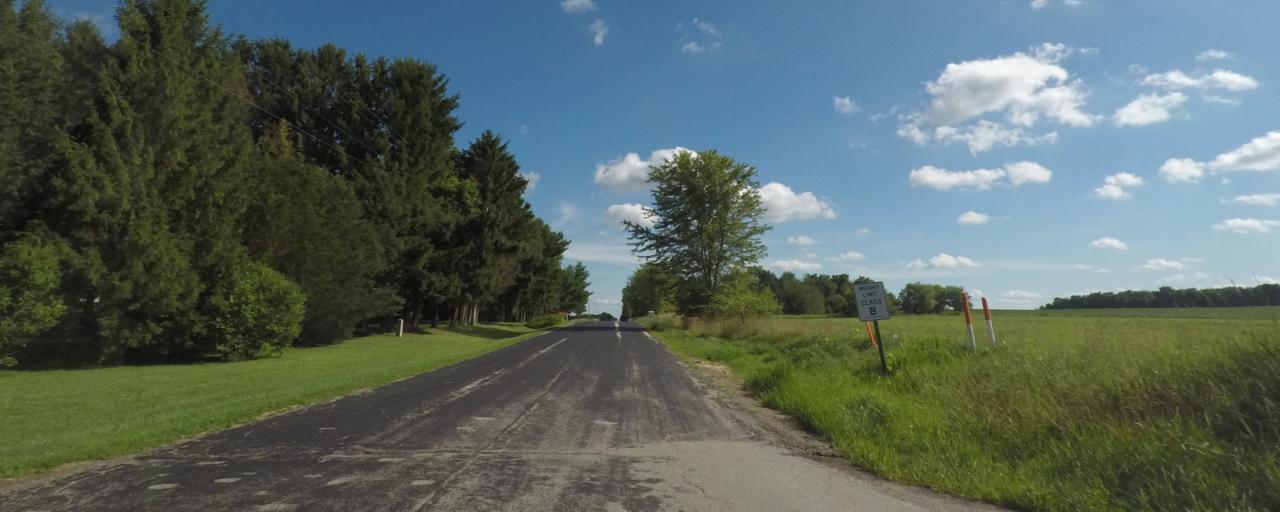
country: US
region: Wisconsin
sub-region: Rock County
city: Edgerton
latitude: 42.8615
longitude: -89.1320
